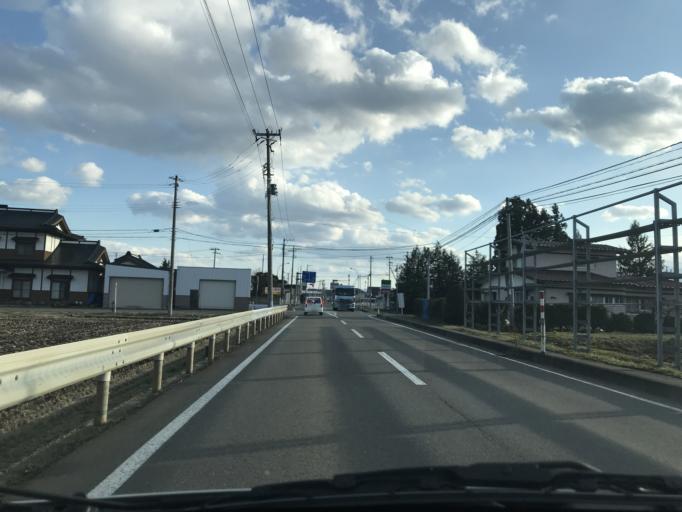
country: JP
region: Iwate
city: Kitakami
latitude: 39.3060
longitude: 141.0340
